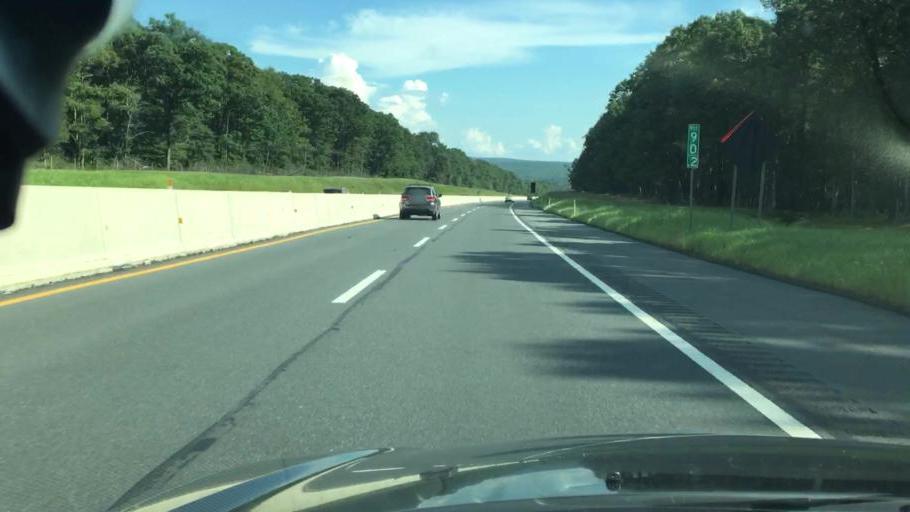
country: US
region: Pennsylvania
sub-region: Carbon County
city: Towamensing Trails
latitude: 41.0257
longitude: -75.6487
